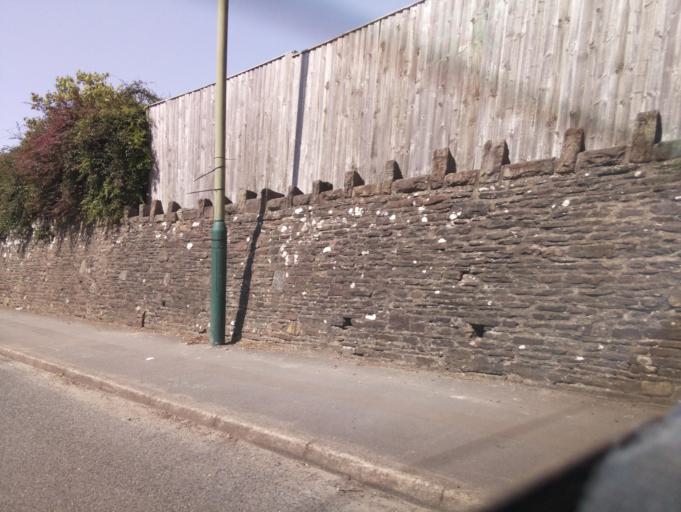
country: GB
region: Wales
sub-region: Caerphilly County Borough
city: Caerphilly
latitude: 51.5836
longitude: -3.2328
